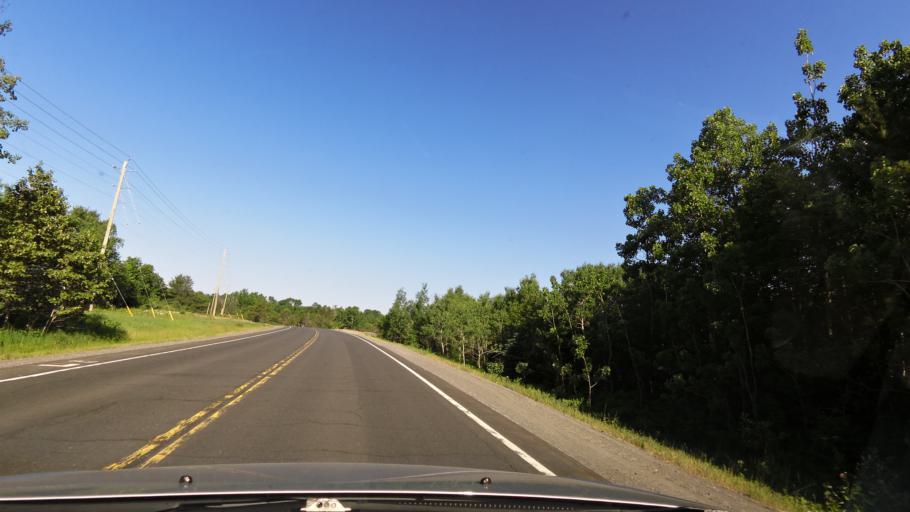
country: CA
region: Ontario
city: Greater Sudbury
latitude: 46.1064
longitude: -80.6482
